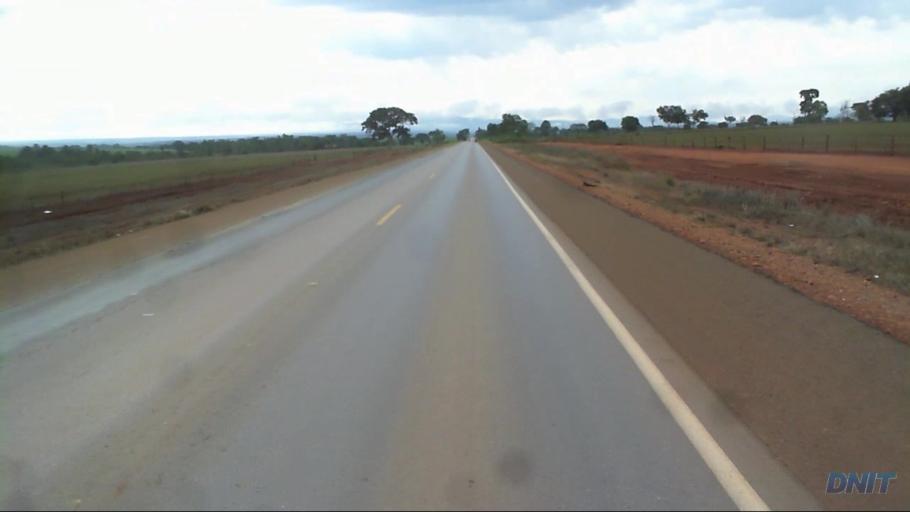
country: BR
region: Goias
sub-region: Uruacu
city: Uruacu
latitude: -14.7049
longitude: -49.1145
